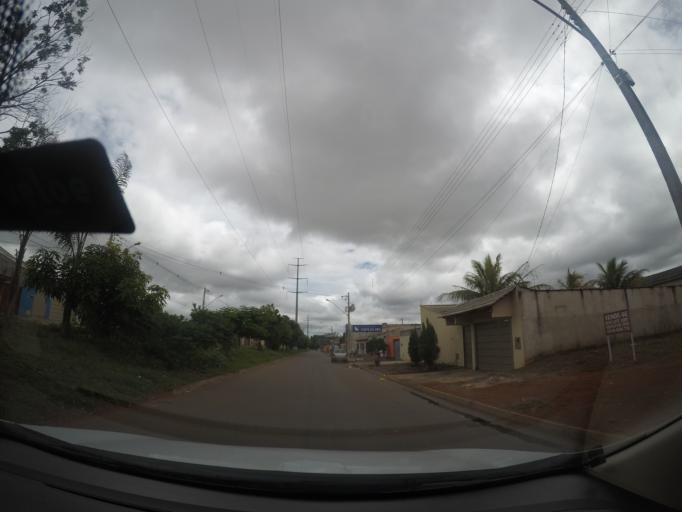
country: BR
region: Goias
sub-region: Goiania
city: Goiania
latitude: -16.7316
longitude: -49.3586
